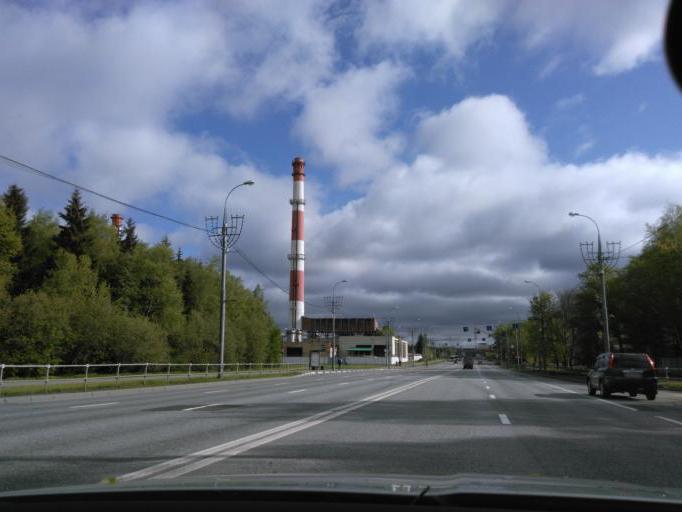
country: RU
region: Moscow
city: Zelenograd
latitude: 56.0025
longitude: 37.1962
